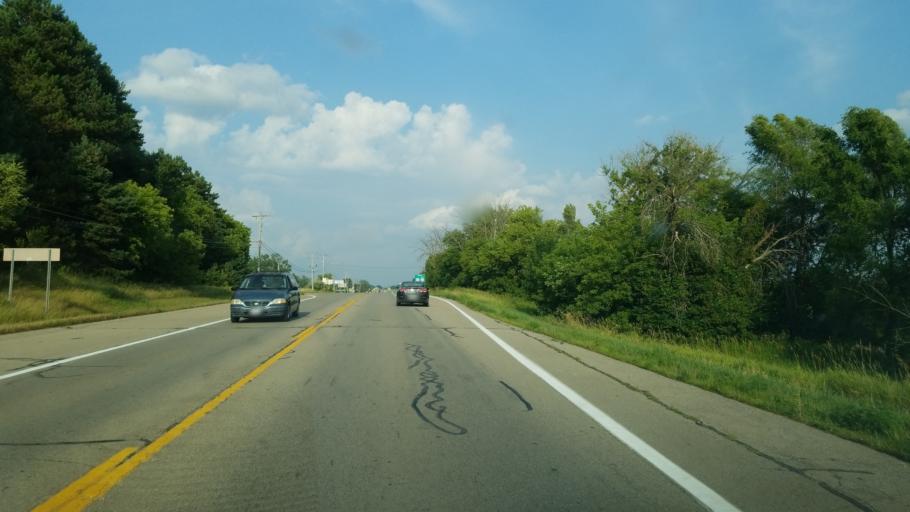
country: US
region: Michigan
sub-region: Gratiot County
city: Alma
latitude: 43.4079
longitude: -84.6743
